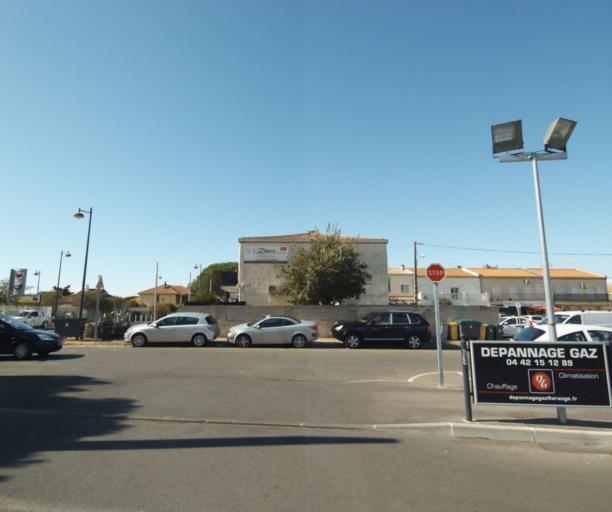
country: FR
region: Provence-Alpes-Cote d'Azur
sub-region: Departement des Bouches-du-Rhone
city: Saint-Victoret
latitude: 43.4167
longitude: 5.2427
